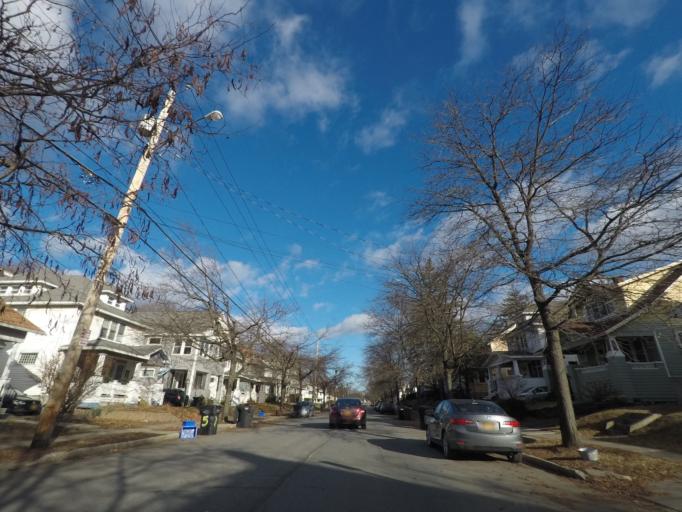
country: US
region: New York
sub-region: Albany County
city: Green Island
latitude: 42.7415
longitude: -73.6742
